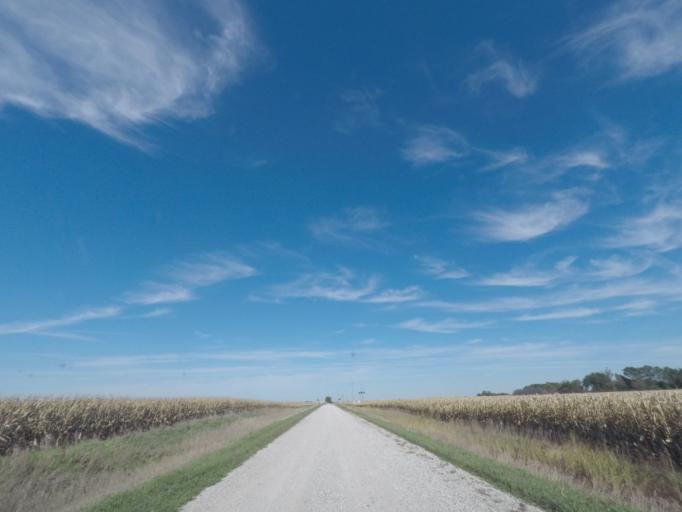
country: US
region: Iowa
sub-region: Story County
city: Nevada
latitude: 42.0172
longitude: -93.3573
